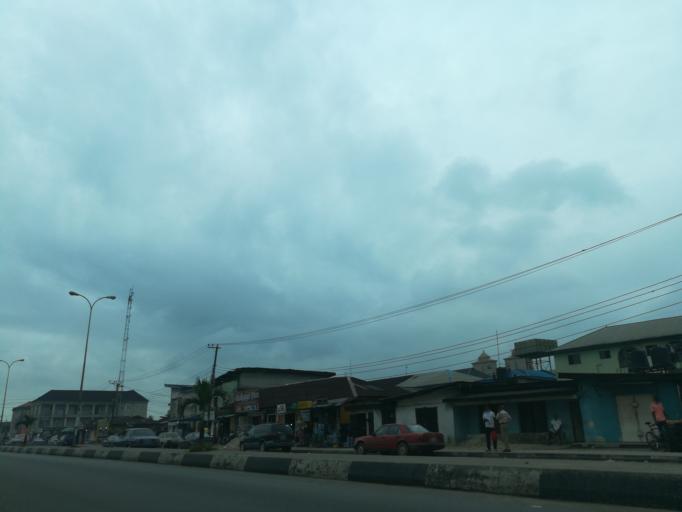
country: NG
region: Rivers
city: Port Harcourt
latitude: 4.8290
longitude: 7.0249
